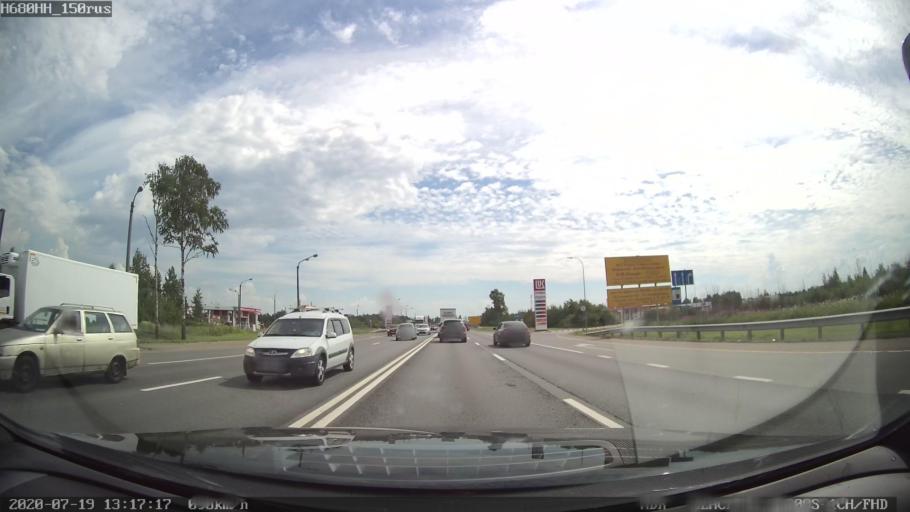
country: RU
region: St.-Petersburg
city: Kolpino
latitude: 59.7099
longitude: 30.5684
